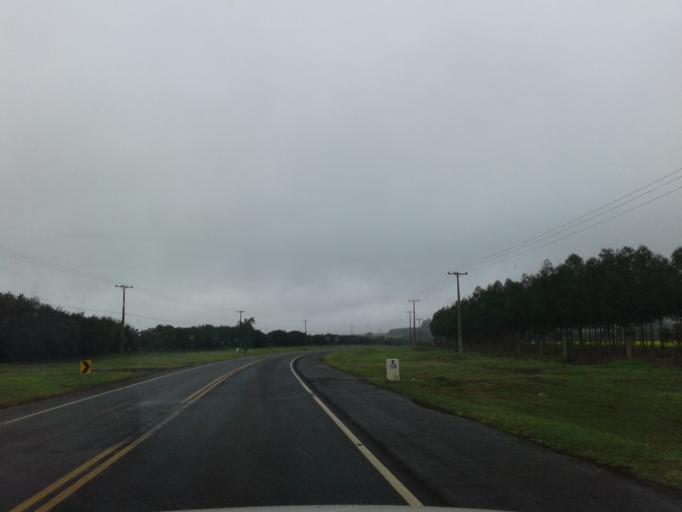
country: PY
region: Alto Parana
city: Naranjal
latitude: -26.1335
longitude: -55.1599
